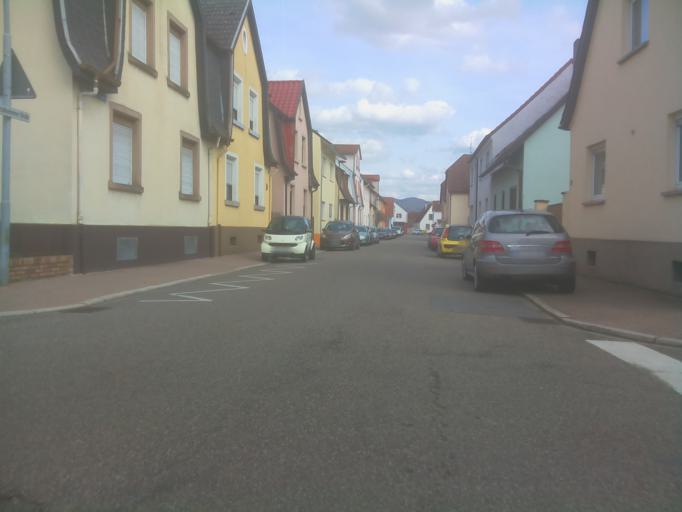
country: DE
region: Baden-Wuerttemberg
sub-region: Karlsruhe Region
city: Heddesheim
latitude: 49.5072
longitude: 8.5972
